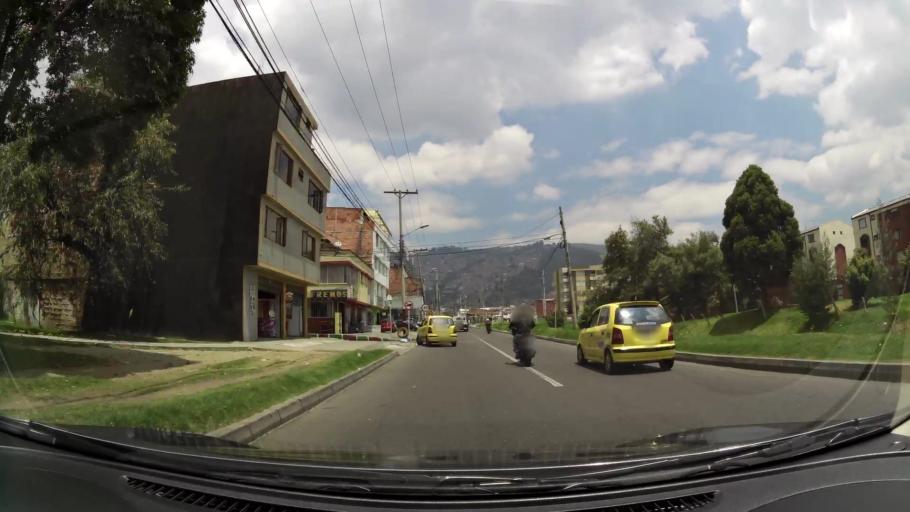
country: CO
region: Cundinamarca
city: La Calera
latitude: 4.7385
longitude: -74.0334
